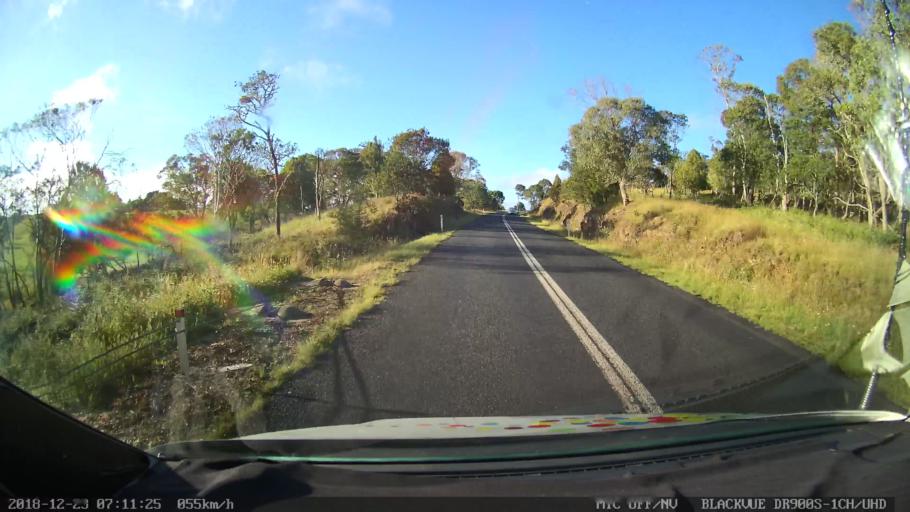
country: AU
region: New South Wales
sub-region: Bellingen
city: Dorrigo
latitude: -30.4029
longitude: 152.3471
